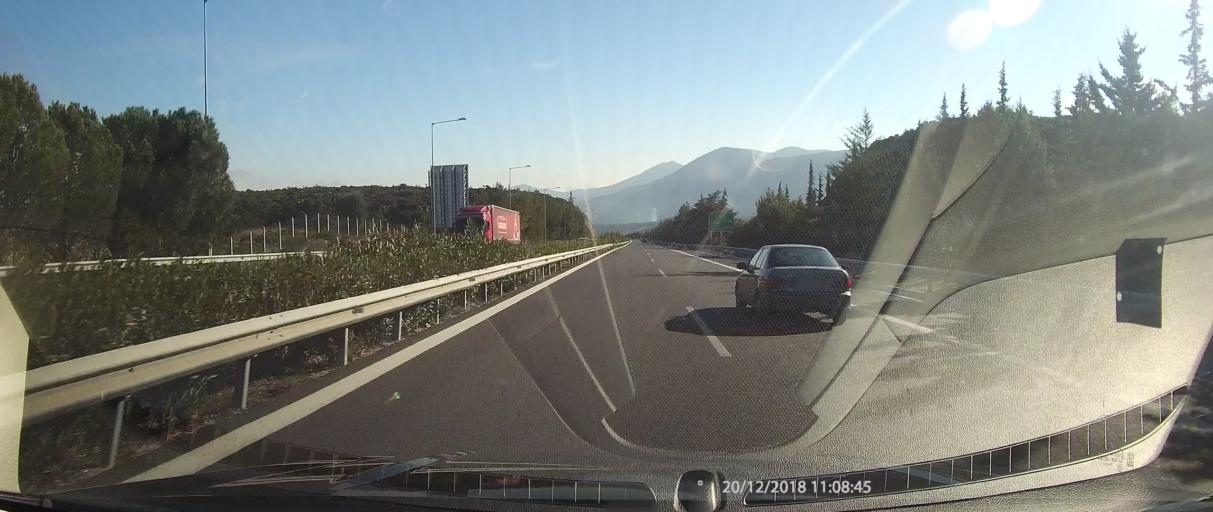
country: GR
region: Peloponnese
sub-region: Nomos Korinthias
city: Ayios Vasilios
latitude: 37.8028
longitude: 22.7418
